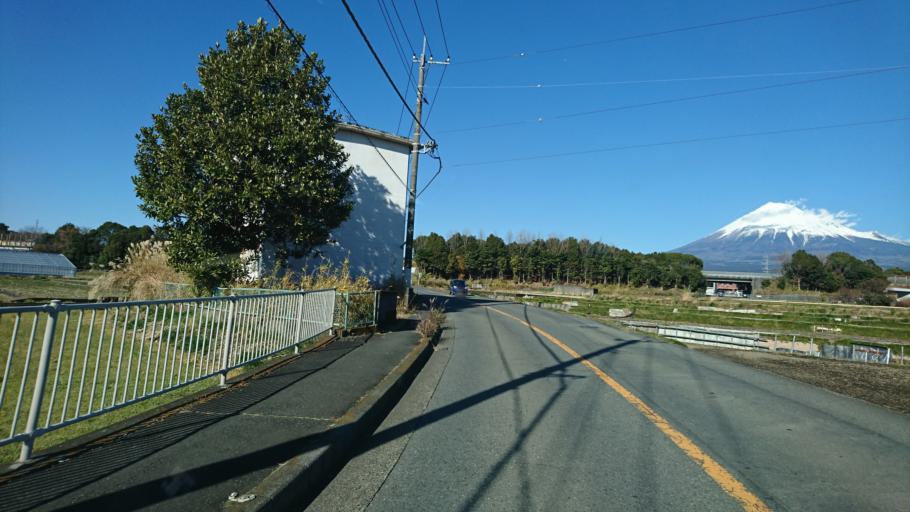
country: JP
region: Shizuoka
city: Fuji
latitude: 35.1757
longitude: 138.6571
